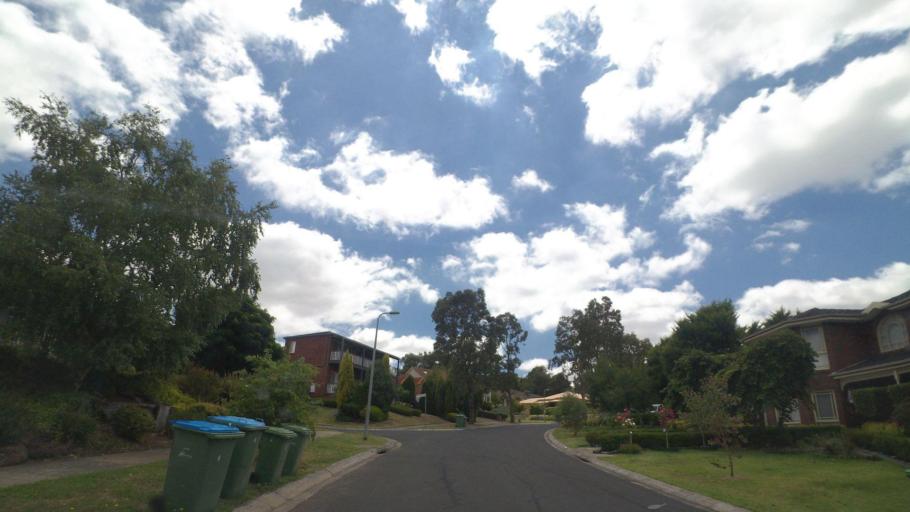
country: AU
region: Victoria
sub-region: Maroondah
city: Croydon Hills
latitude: -37.7676
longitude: 145.2706
